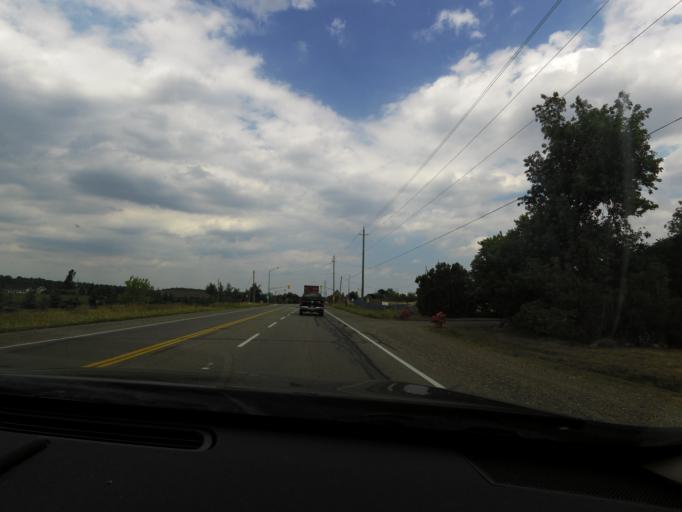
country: CA
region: Ontario
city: Brampton
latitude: 43.7822
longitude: -79.8691
